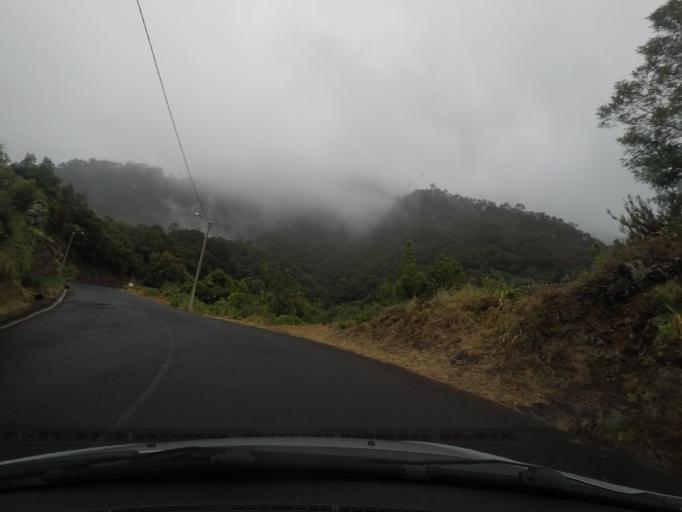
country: PT
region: Madeira
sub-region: Santana
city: Santana
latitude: 32.7843
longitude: -16.8585
